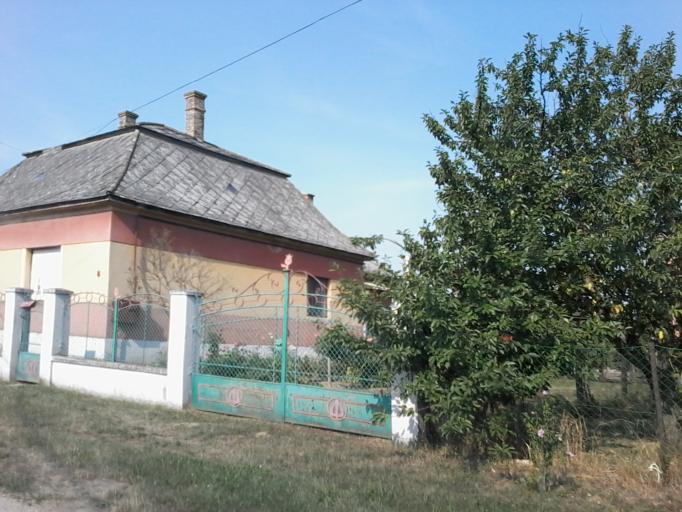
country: HU
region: Vas
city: Janoshaza
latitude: 47.0530
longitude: 17.1380
